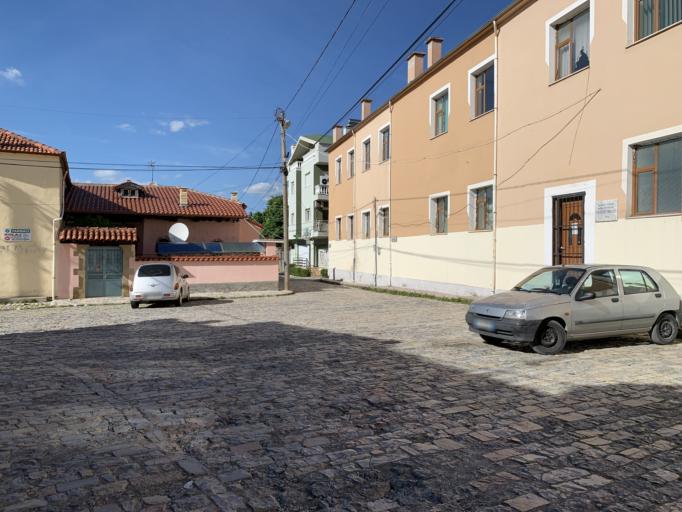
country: AL
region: Korce
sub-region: Rrethi i Korces
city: Korce
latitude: 40.6160
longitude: 20.7830
